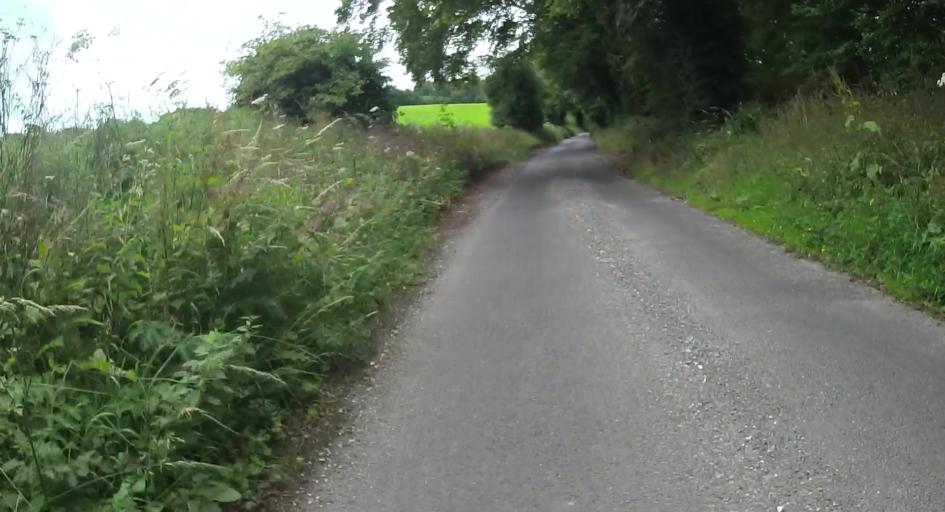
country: GB
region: England
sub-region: Hampshire
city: Basingstoke
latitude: 51.2253
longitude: -1.0908
